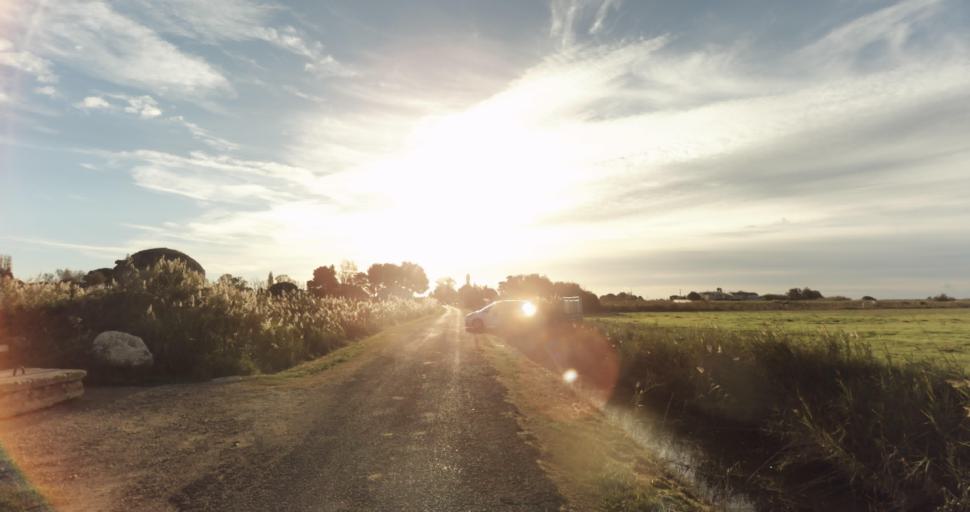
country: FR
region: Languedoc-Roussillon
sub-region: Departement du Gard
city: Aigues-Mortes
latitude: 43.5641
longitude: 4.1952
